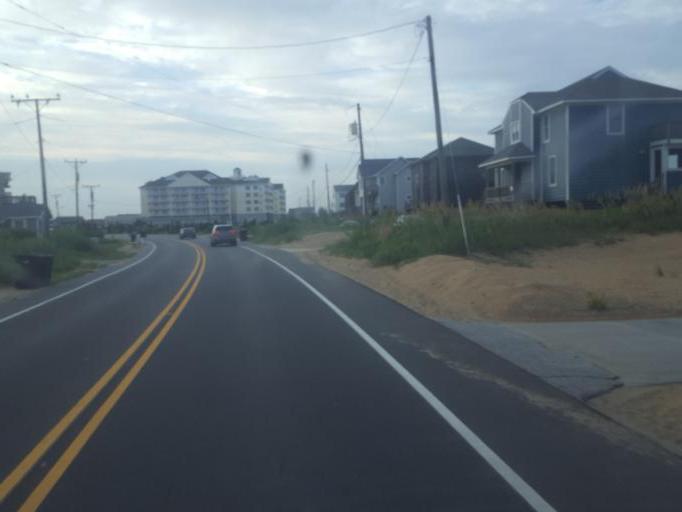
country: US
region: North Carolina
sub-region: Dare County
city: Kitty Hawk
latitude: 36.0984
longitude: -75.7100
